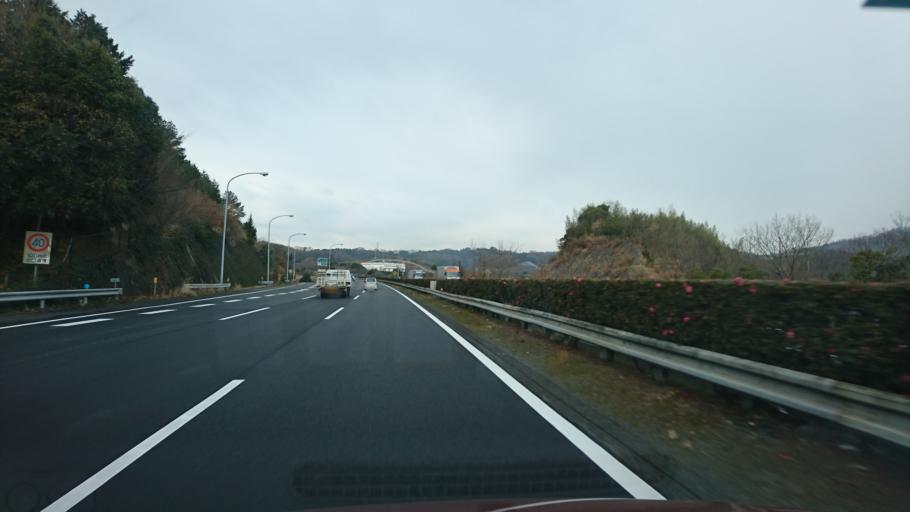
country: JP
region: Okayama
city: Kurashiki
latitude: 34.6257
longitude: 133.7735
